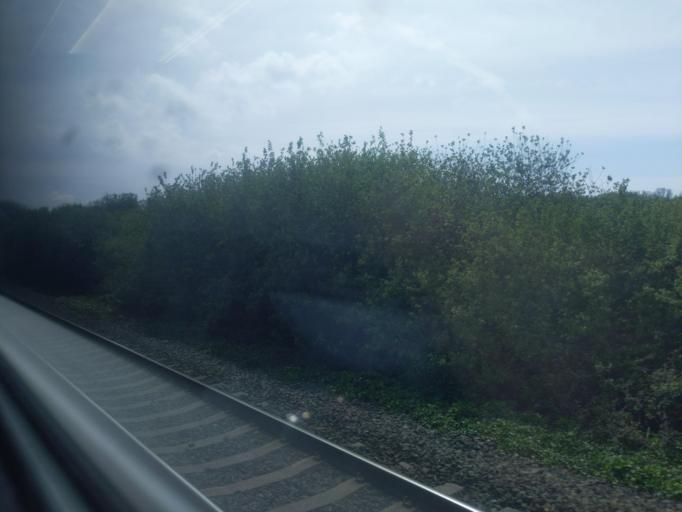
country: GB
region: England
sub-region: Cornwall
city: Marazion
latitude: 50.1523
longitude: -5.4606
